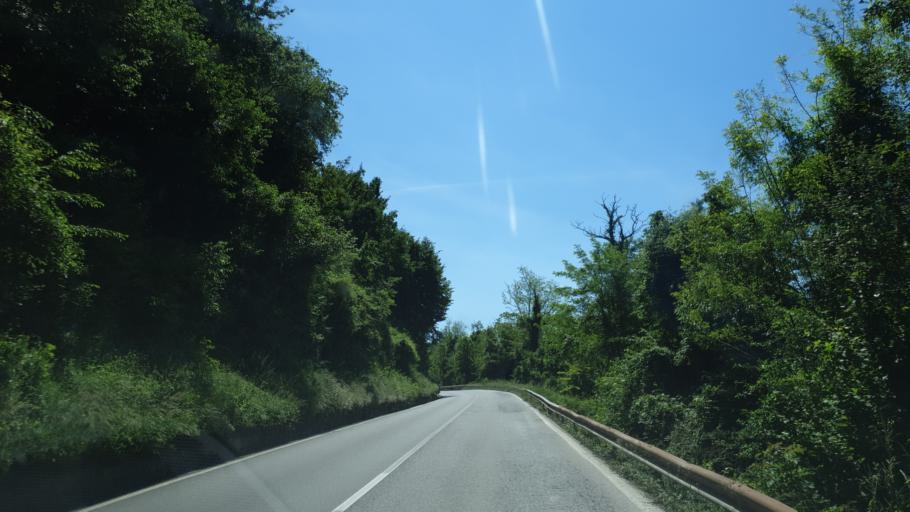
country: IT
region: Lombardy
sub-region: Provincia di Bergamo
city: Cisano Bergamasco
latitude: 45.7534
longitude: 9.4597
